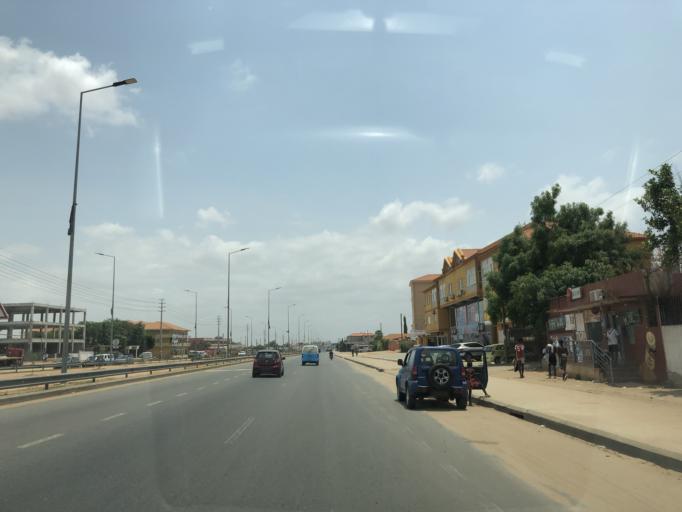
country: AO
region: Luanda
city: Luanda
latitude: -8.9234
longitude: 13.2624
